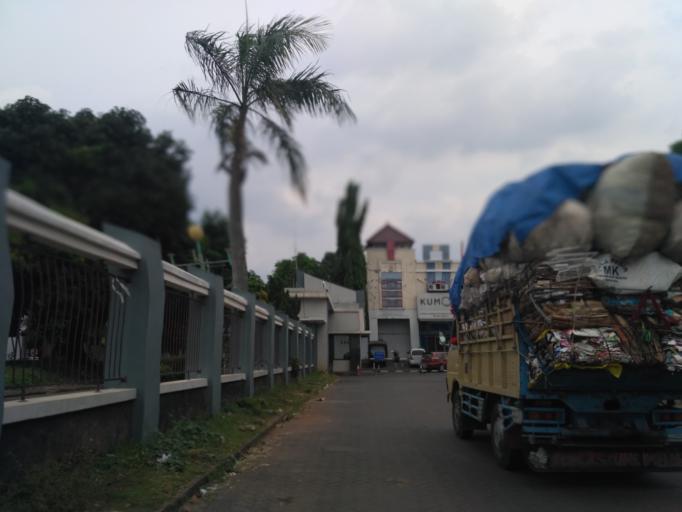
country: ID
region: Central Java
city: Semarang
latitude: -7.0660
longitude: 110.4191
